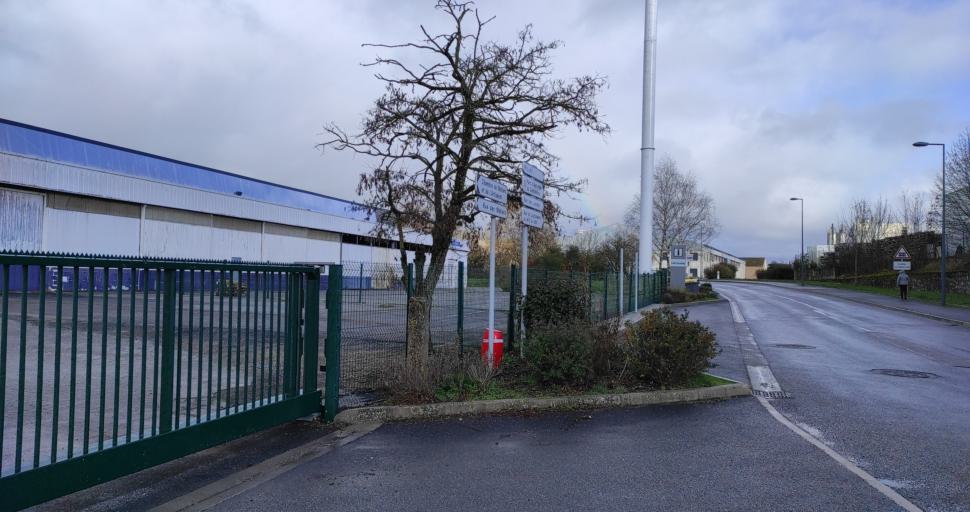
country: FR
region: Midi-Pyrenees
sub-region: Departement de l'Aveyron
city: Sainte-Radegonde
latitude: 44.3613
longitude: 2.6067
